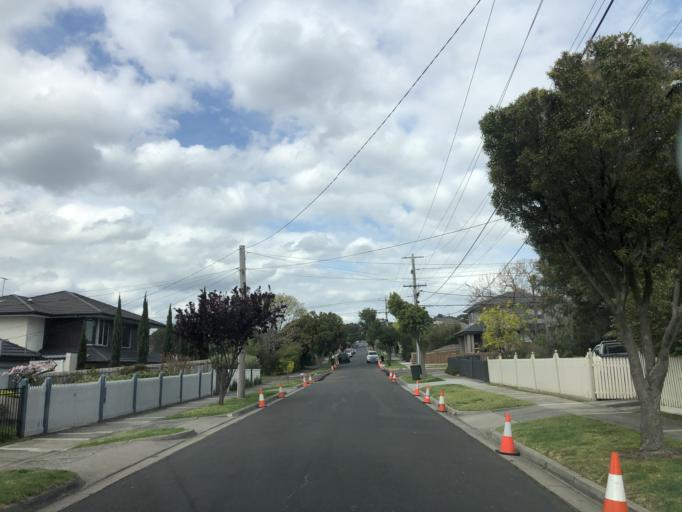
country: AU
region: Victoria
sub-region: Monash
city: Ashwood
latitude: -37.8620
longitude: 145.1083
